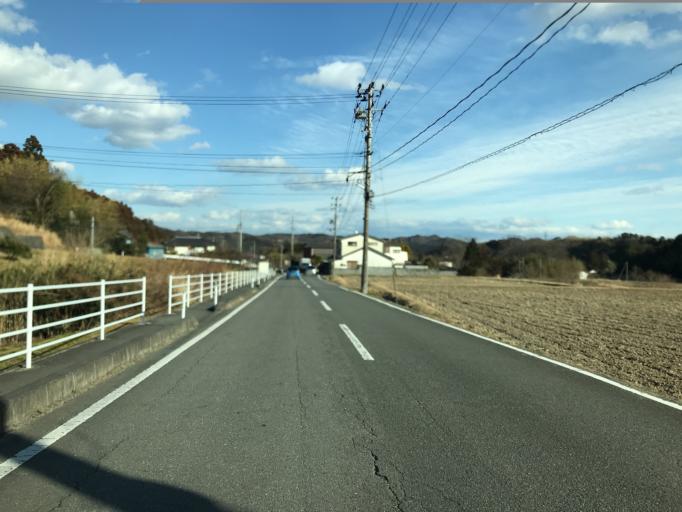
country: JP
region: Fukushima
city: Iwaki
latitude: 37.1263
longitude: 140.8485
